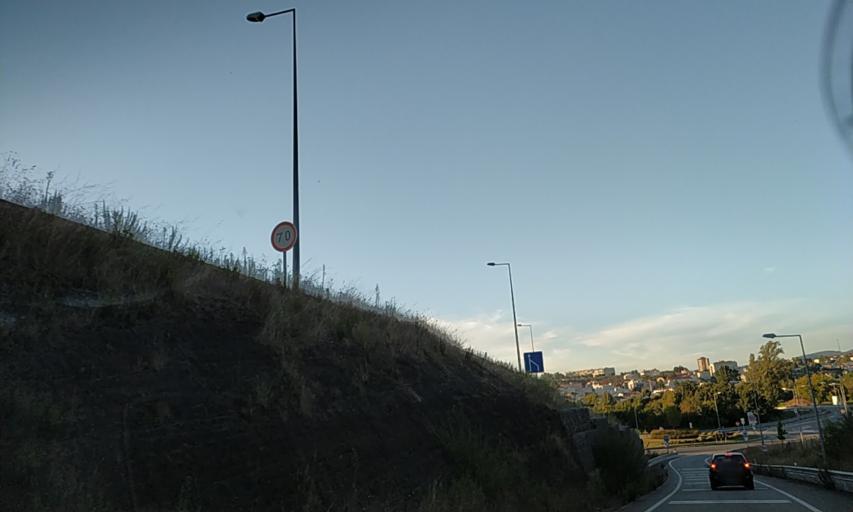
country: PT
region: Aveiro
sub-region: Agueda
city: Agueda
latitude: 40.5648
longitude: -8.4495
